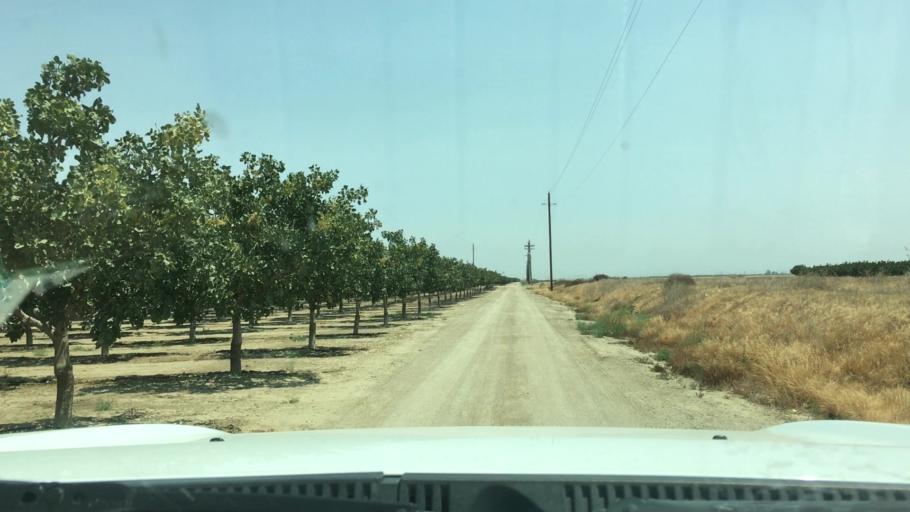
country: US
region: California
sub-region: Kern County
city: Wasco
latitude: 35.6814
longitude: -119.4223
